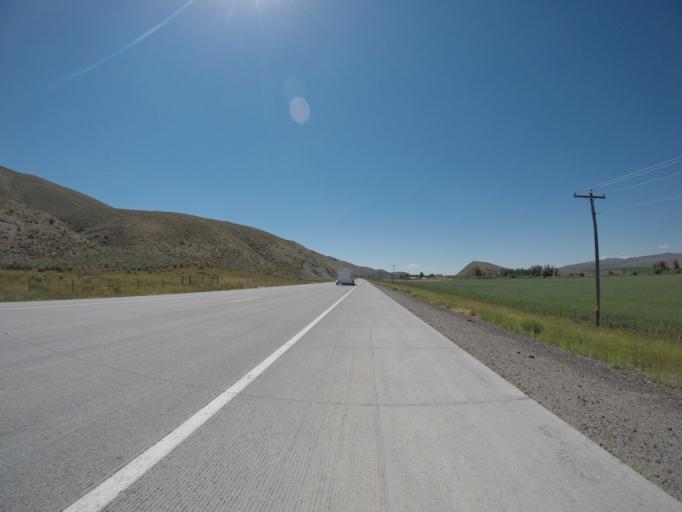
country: US
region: Idaho
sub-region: Bear Lake County
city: Montpelier
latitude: 42.1459
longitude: -110.9764
